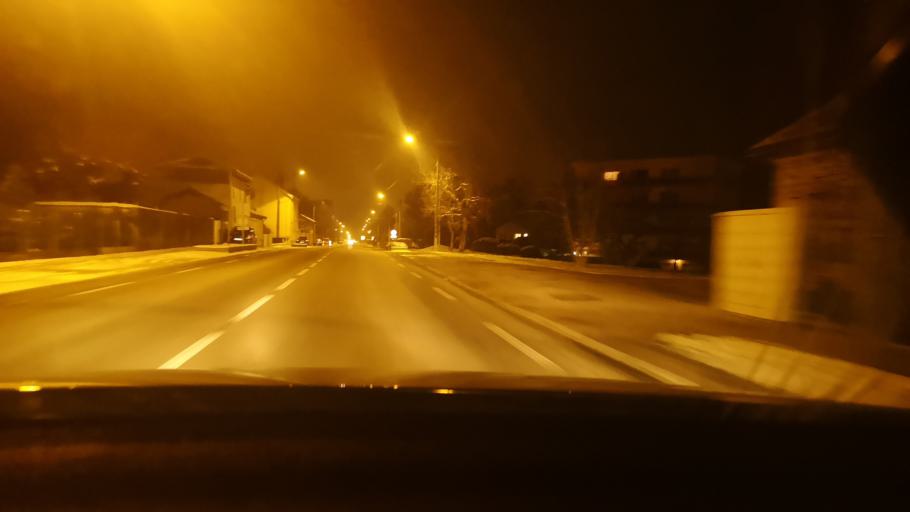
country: FR
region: Rhone-Alpes
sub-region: Departement de l'Ain
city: Ceyzeriat
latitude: 46.1798
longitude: 5.3194
